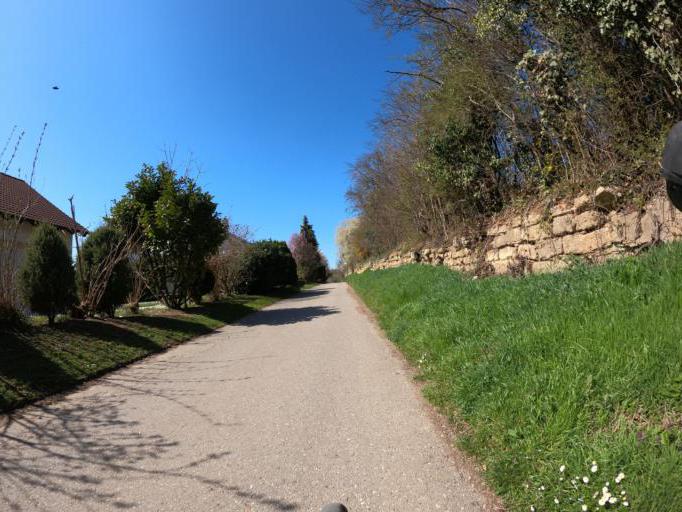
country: DE
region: Baden-Wuerttemberg
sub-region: Tuebingen Region
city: Rottenburg
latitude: 48.4733
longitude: 8.9227
